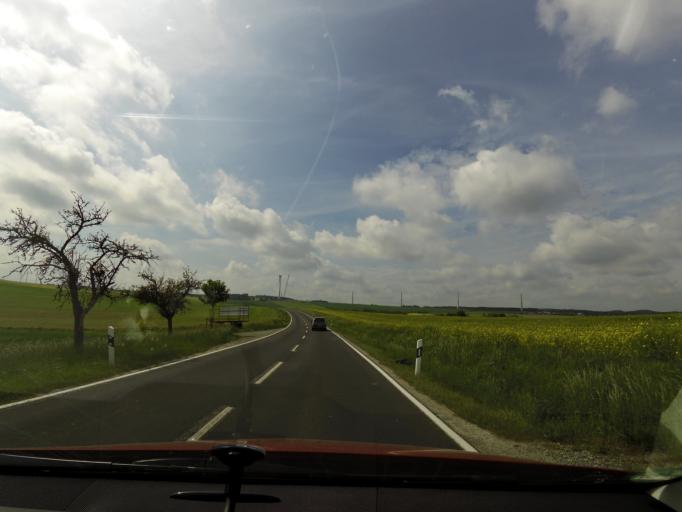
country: DE
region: Thuringia
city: Mihla
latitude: 51.0695
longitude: 10.3243
